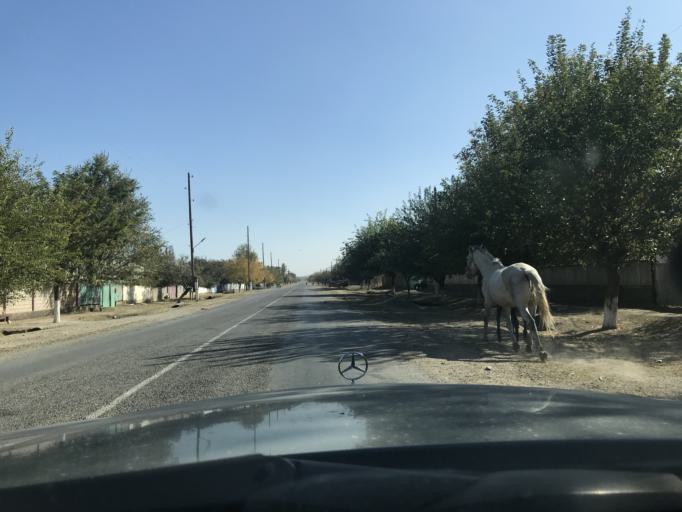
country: KZ
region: Ongtustik Qazaqstan
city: Sastobe
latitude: 42.5464
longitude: 69.9221
